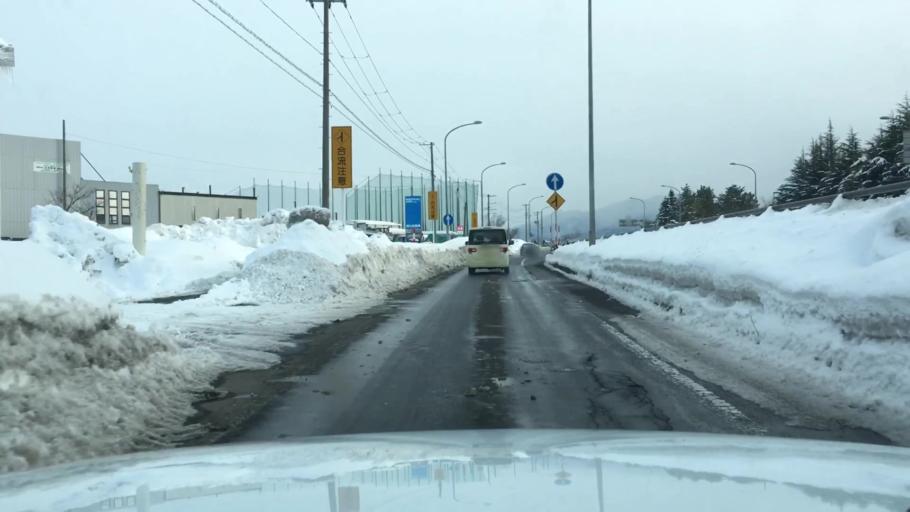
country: JP
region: Aomori
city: Hirosaki
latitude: 40.5938
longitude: 140.5052
